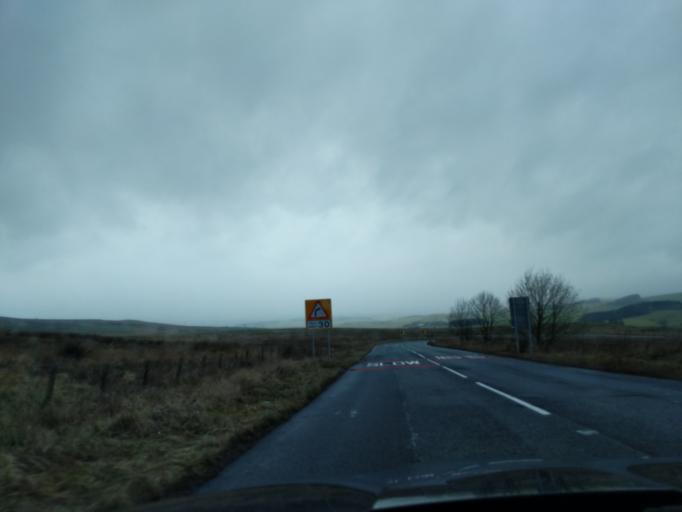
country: GB
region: England
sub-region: Northumberland
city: Otterburn
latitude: 55.2119
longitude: -2.1080
